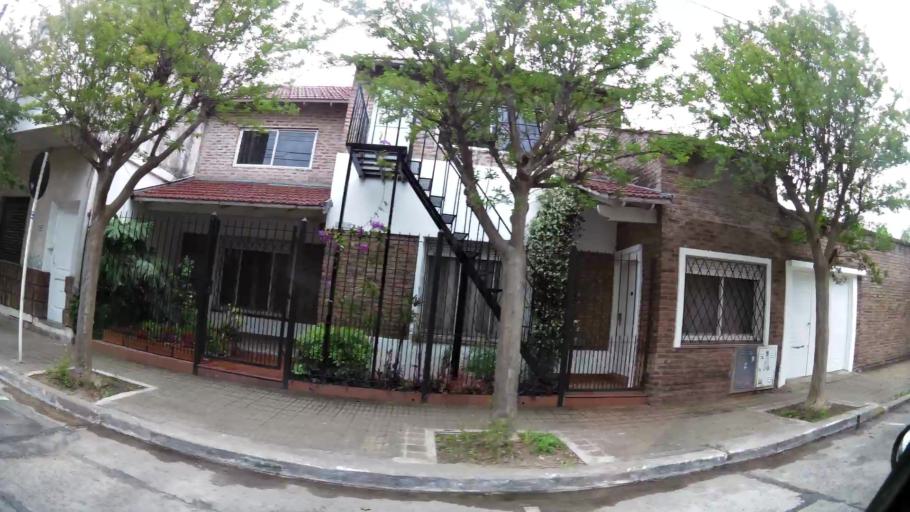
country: AR
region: Buenos Aires
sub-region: Partido de Quilmes
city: Quilmes
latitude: -34.7614
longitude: -58.2041
